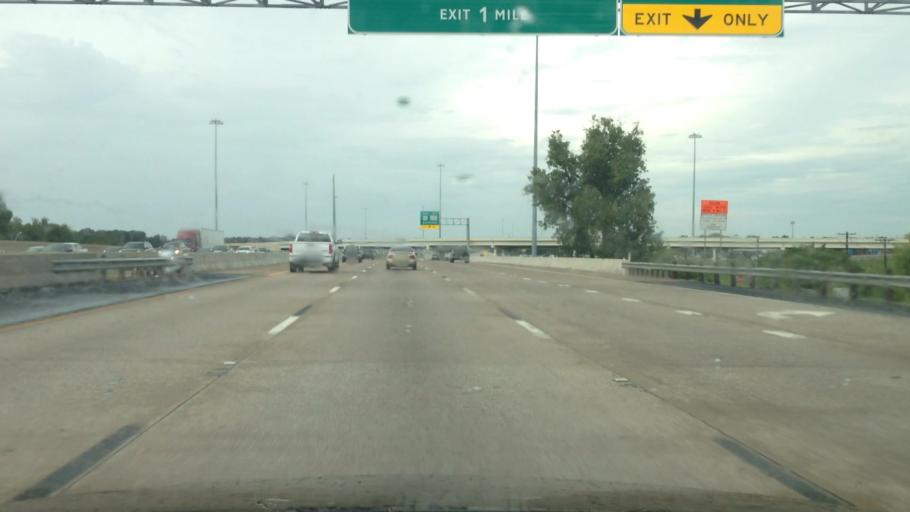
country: US
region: Texas
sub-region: Tarrant County
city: Grapevine
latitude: 32.9014
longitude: -97.0991
